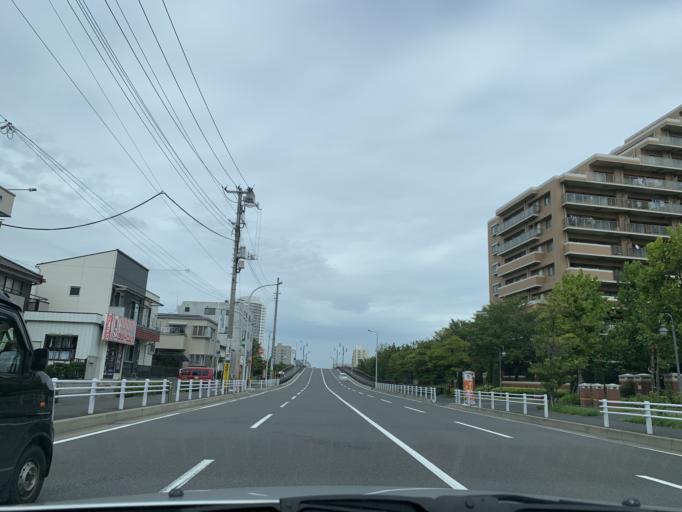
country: JP
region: Tokyo
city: Urayasu
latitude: 35.6382
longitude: 139.9158
